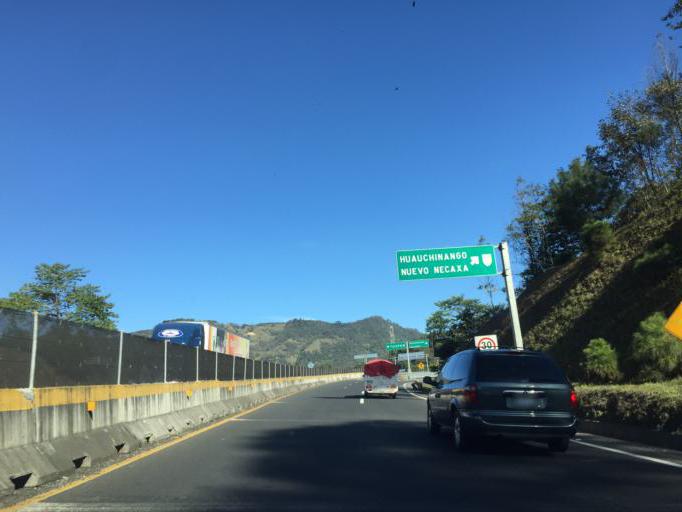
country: MX
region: Puebla
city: Huauchinango
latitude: 20.1873
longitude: -98.0295
